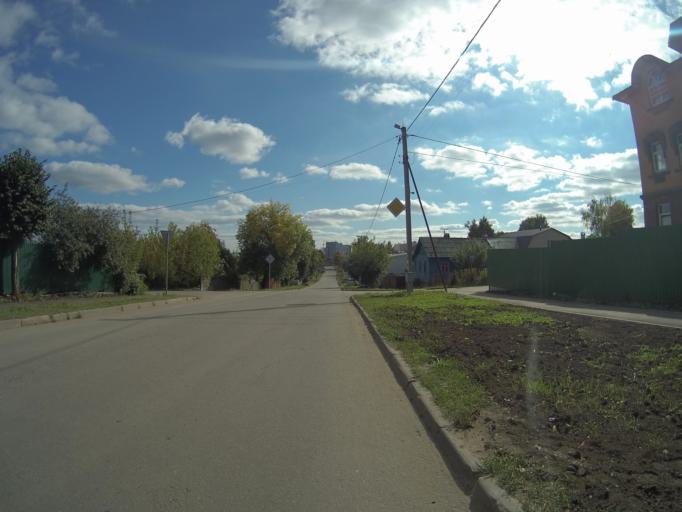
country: RU
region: Vladimir
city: Vladimir
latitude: 56.1154
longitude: 40.3665
